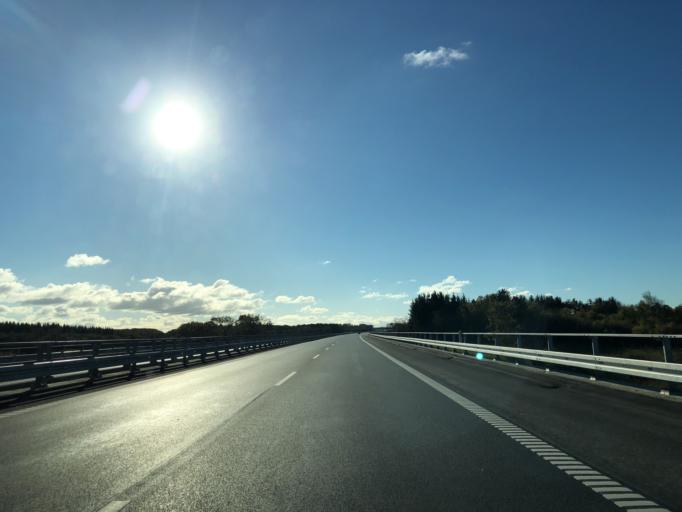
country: DK
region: Central Jutland
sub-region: Herning Kommune
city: Avlum
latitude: 56.3290
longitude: 8.7358
